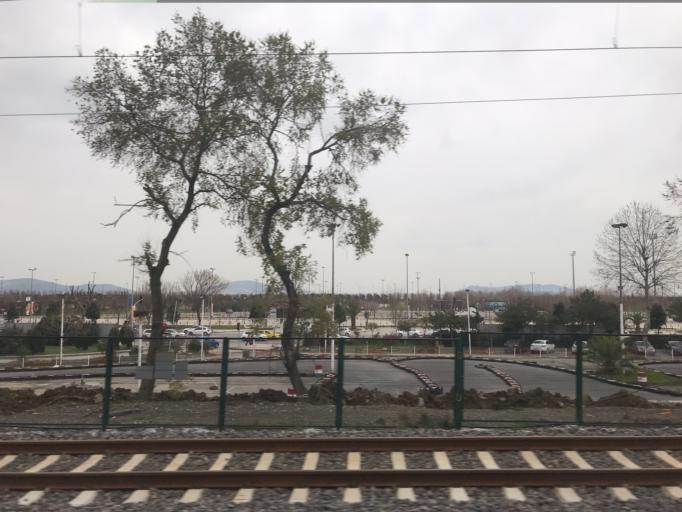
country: TR
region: Istanbul
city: Maltepe
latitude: 40.9294
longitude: 29.1216
